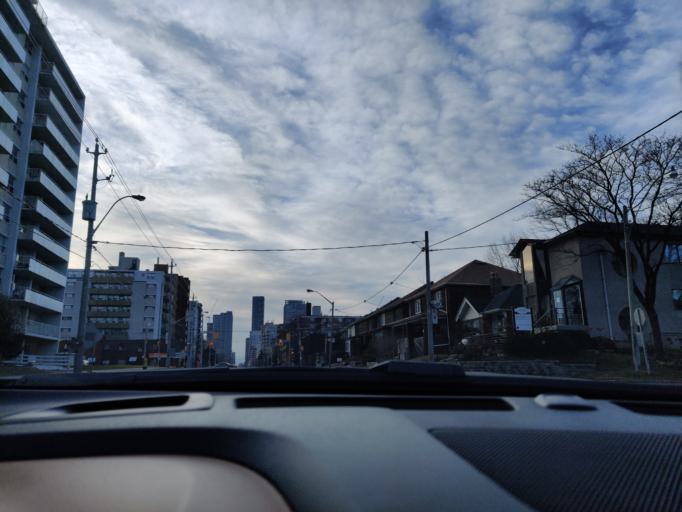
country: CA
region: Ontario
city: Toronto
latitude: 43.7103
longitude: -79.3810
